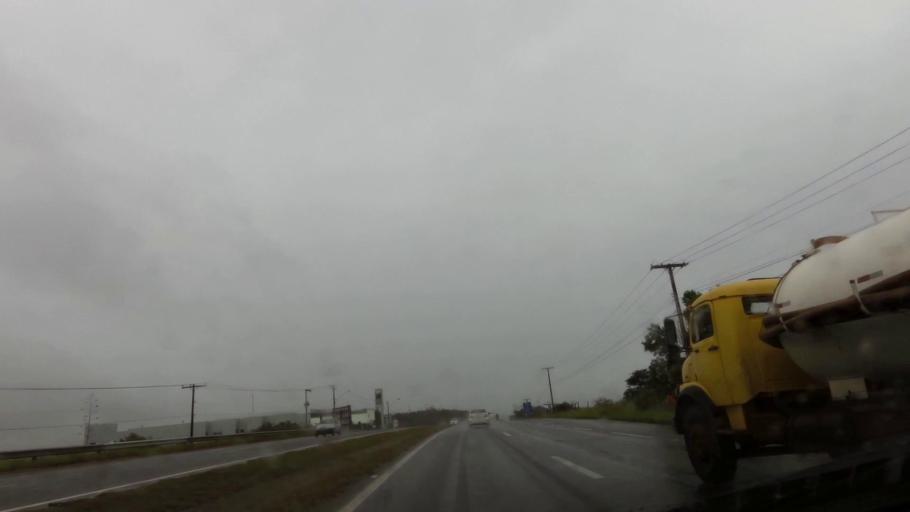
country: BR
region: Espirito Santo
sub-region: Vitoria
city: Vitoria
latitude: -20.4706
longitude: -40.3511
